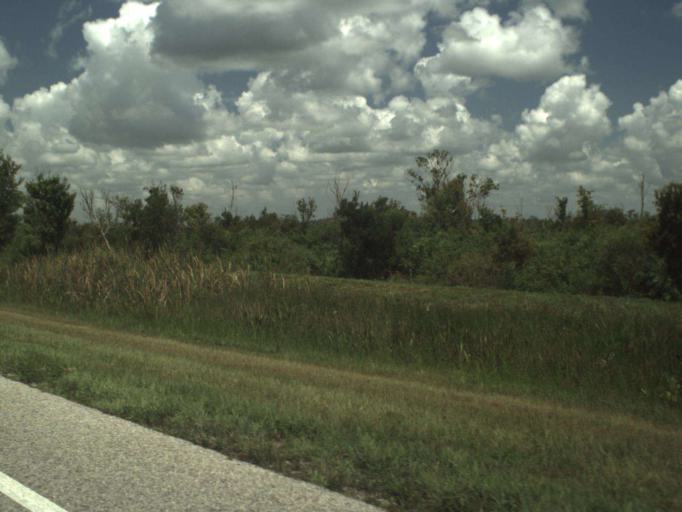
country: US
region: Florida
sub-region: Indian River County
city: Fellsmere
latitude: 27.6417
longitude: -80.7390
